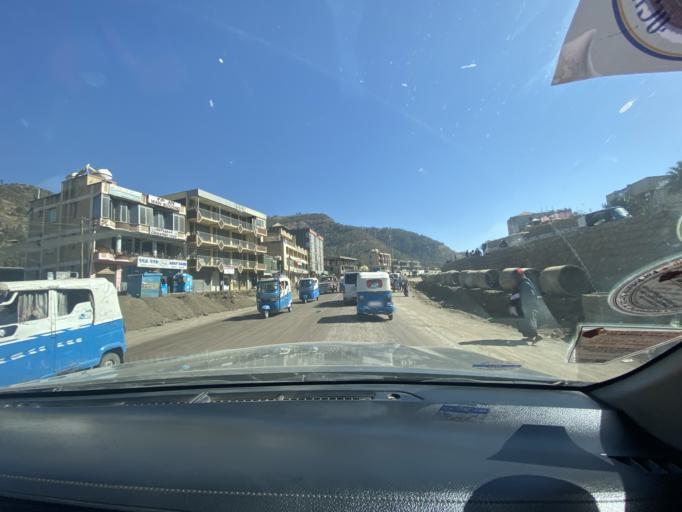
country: ET
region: Amhara
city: Robit
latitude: 11.8326
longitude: 39.6032
